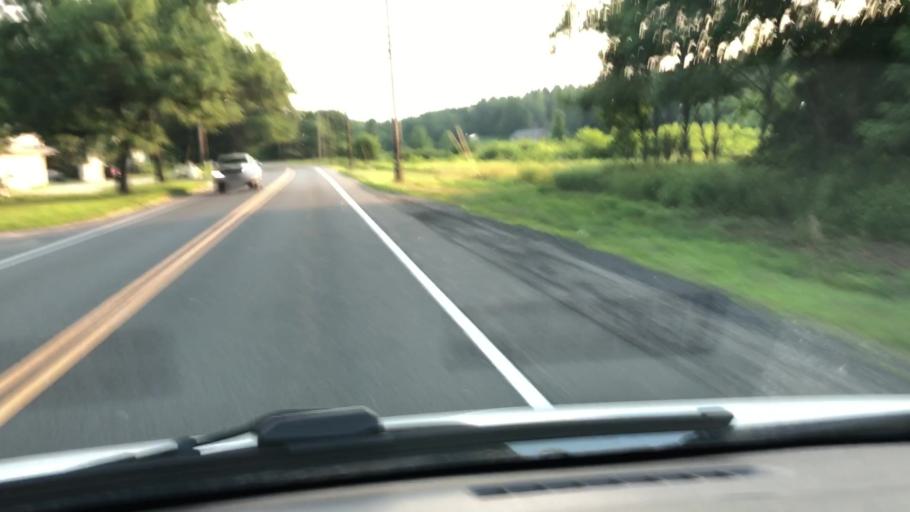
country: US
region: Massachusetts
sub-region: Hampshire County
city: Williamsburg
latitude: 42.3661
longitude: -72.6937
